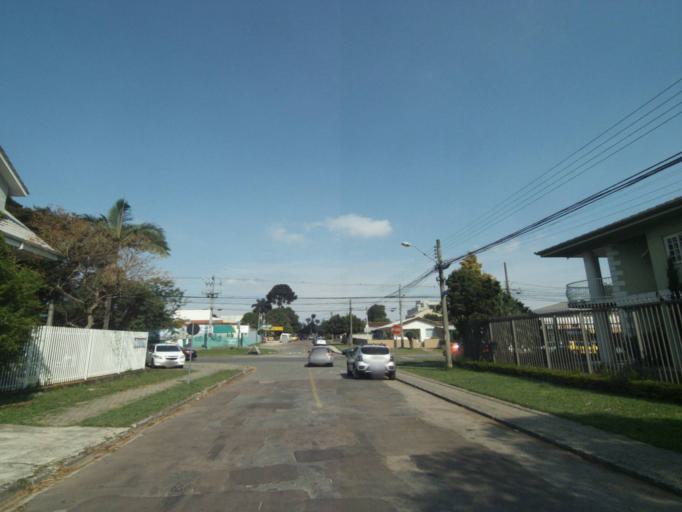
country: BR
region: Parana
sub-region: Curitiba
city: Curitiba
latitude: -25.4828
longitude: -49.3265
